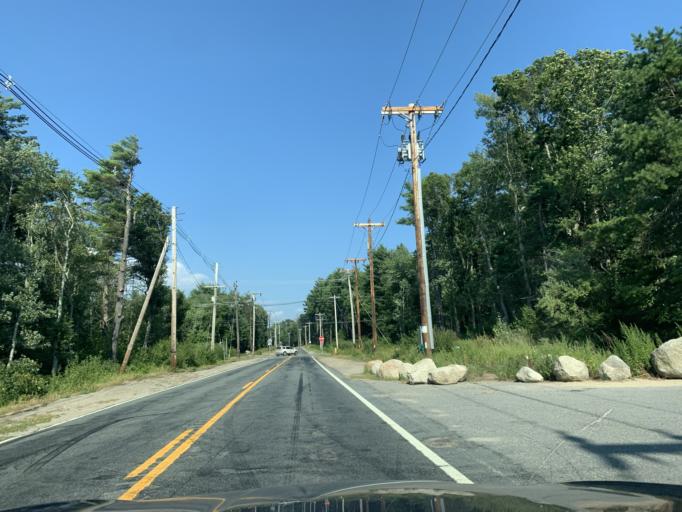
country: US
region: Rhode Island
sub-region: Kent County
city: West Warwick
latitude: 41.6491
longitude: -71.5745
